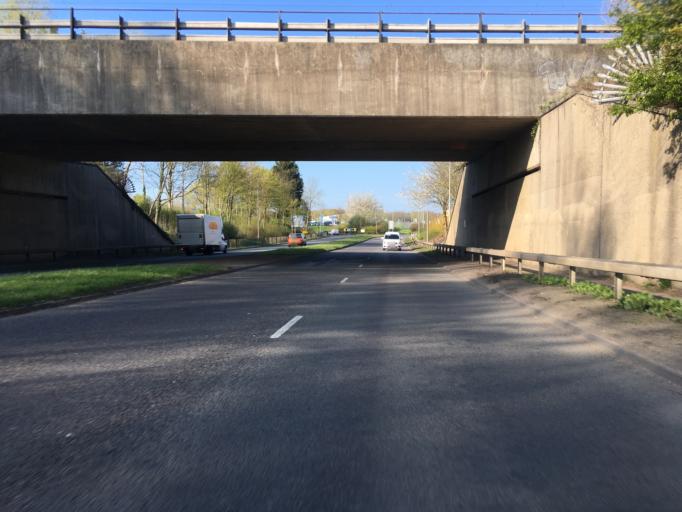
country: GB
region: England
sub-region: Milton Keynes
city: Bradwell
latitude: 52.0505
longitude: -0.7957
